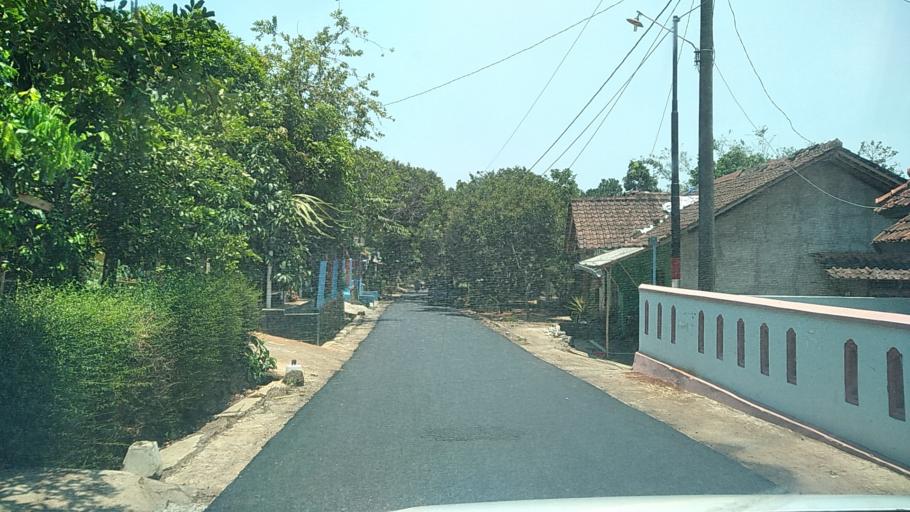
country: ID
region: Central Java
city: Ungaran
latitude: -7.0696
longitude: 110.3704
